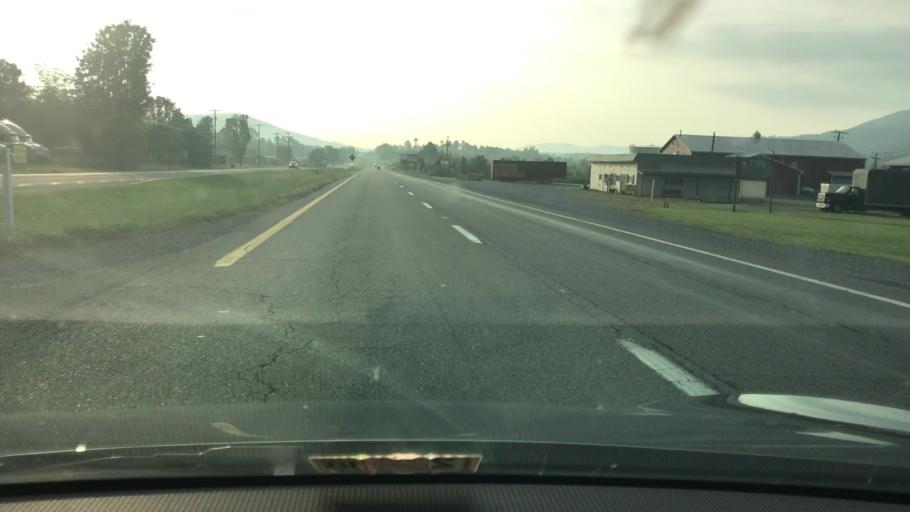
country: US
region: Virginia
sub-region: Botetourt County
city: Blue Ridge
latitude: 37.3856
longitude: -79.7348
